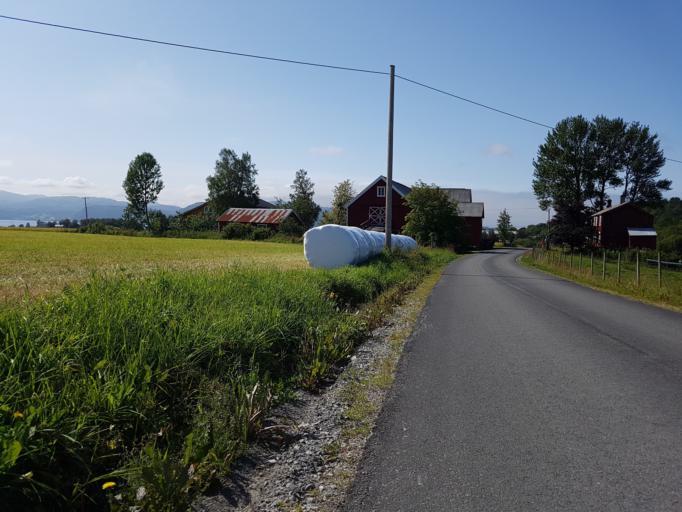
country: NO
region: Sor-Trondelag
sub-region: Agdenes
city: Lensvik
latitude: 63.6300
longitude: 9.8349
